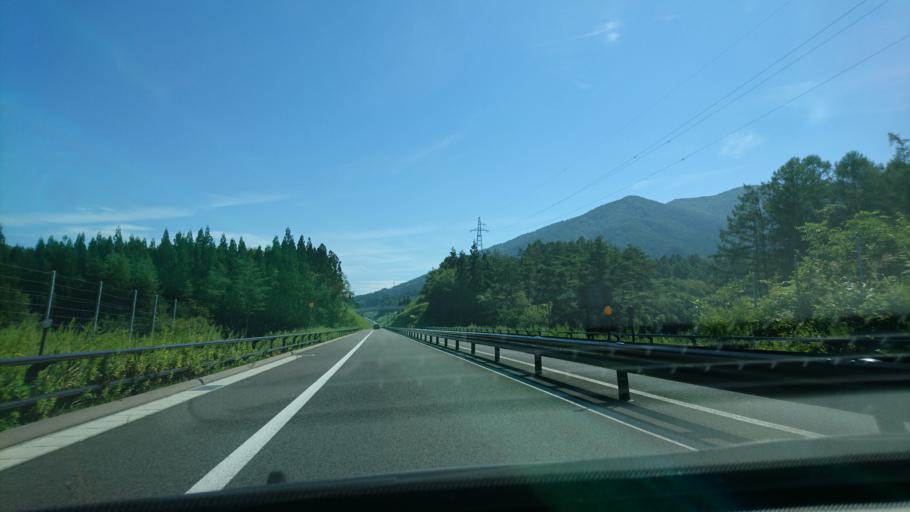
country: JP
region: Iwate
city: Tono
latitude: 39.3176
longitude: 141.4652
